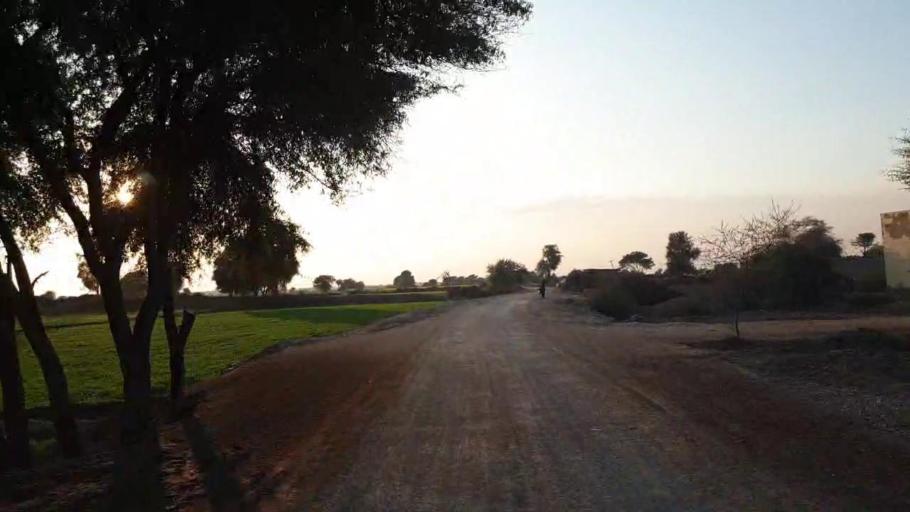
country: PK
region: Sindh
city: Shahpur Chakar
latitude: 26.1589
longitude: 68.5365
